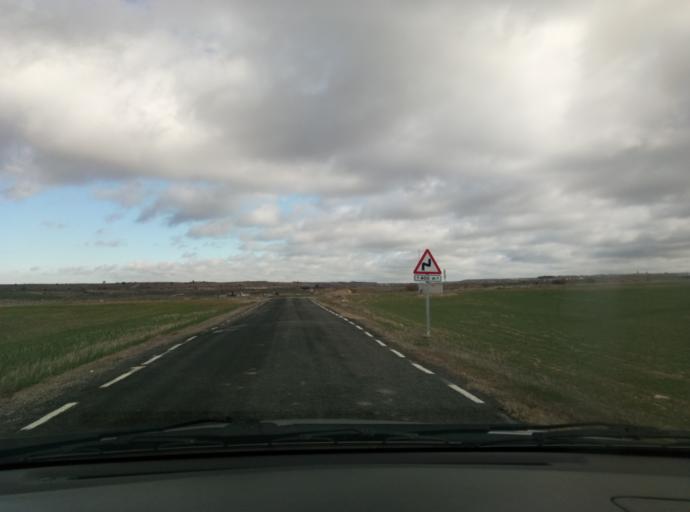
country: ES
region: Catalonia
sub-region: Provincia de Lleida
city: Verdu
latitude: 41.5994
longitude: 1.0999
